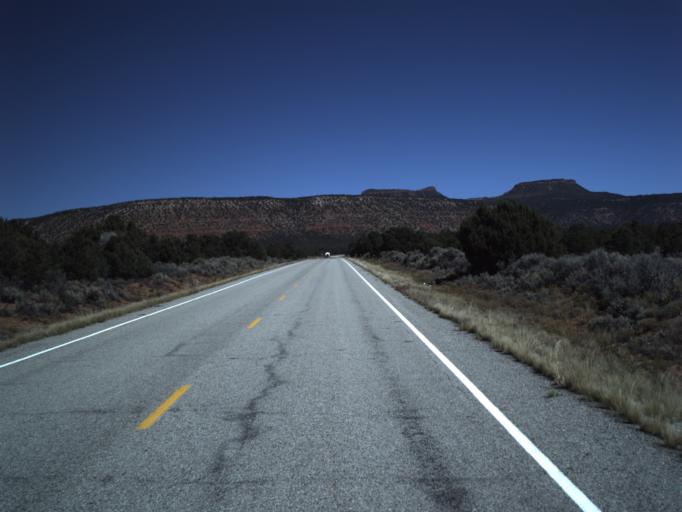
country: US
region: Utah
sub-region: San Juan County
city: Blanding
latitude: 37.5714
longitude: -109.9234
